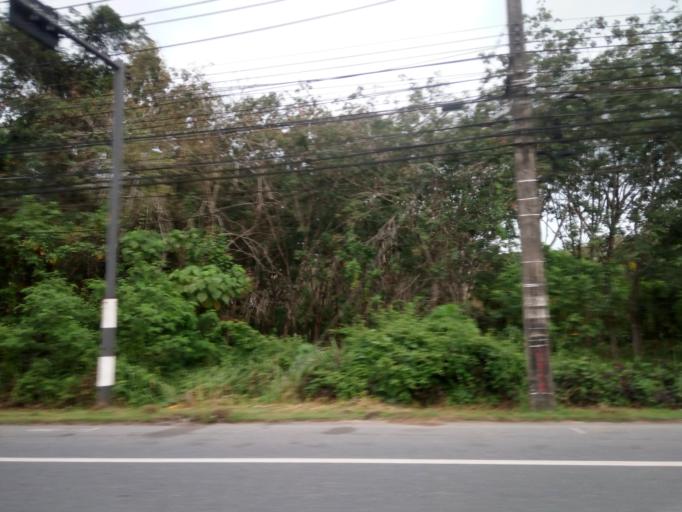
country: TH
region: Phuket
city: Thalang
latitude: 8.1118
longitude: 98.3353
